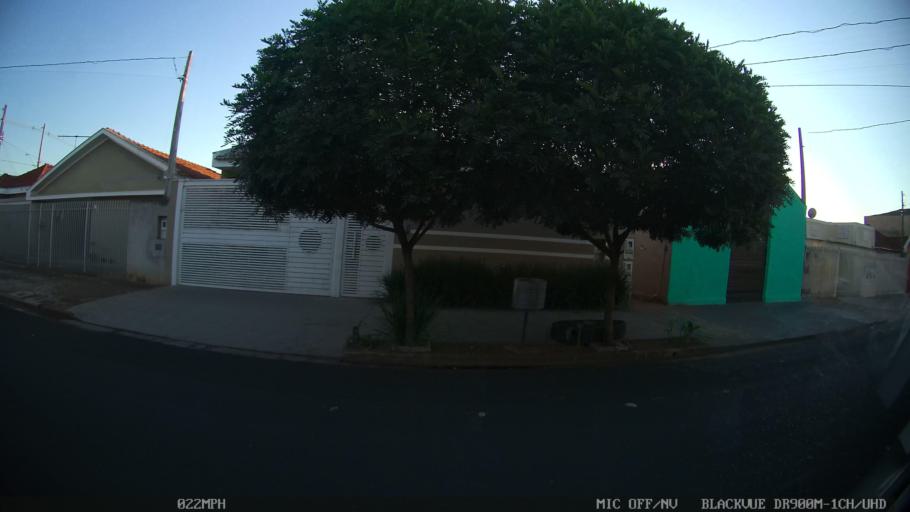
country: BR
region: Sao Paulo
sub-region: Sao Jose Do Rio Preto
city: Sao Jose do Rio Preto
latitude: -20.7920
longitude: -49.3710
